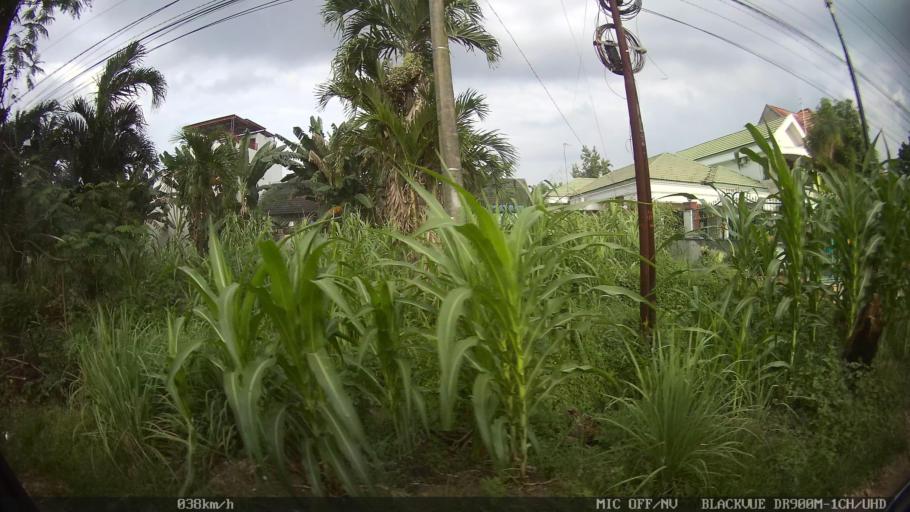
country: ID
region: North Sumatra
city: Sunggal
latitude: 3.5365
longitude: 98.6054
